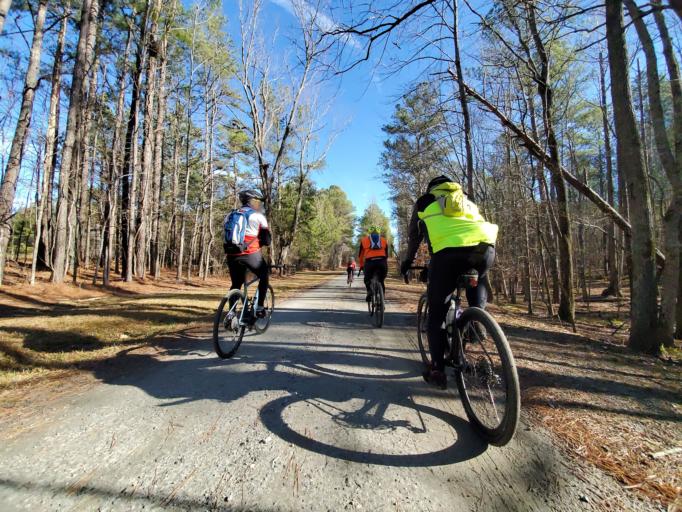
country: US
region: Georgia
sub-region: Fulton County
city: Chattahoochee Hills
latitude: 33.5697
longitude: -84.8052
